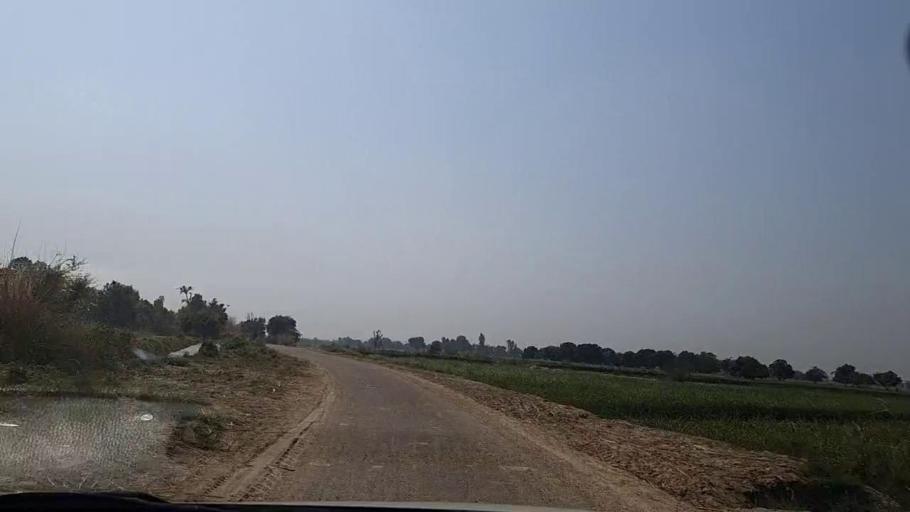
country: PK
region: Sindh
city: Mirpur Khas
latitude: 25.4901
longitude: 69.1965
